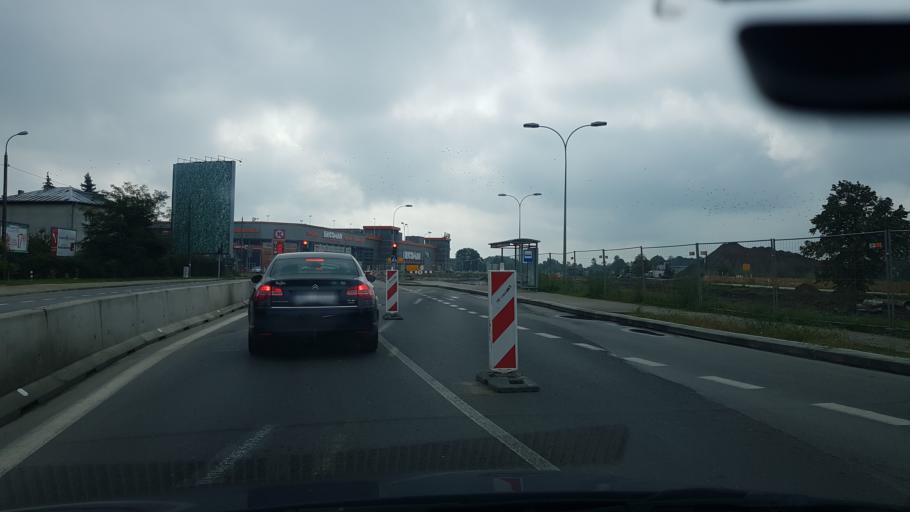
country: PL
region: Masovian Voivodeship
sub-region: Warszawa
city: Wilanow
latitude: 52.1548
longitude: 21.0907
